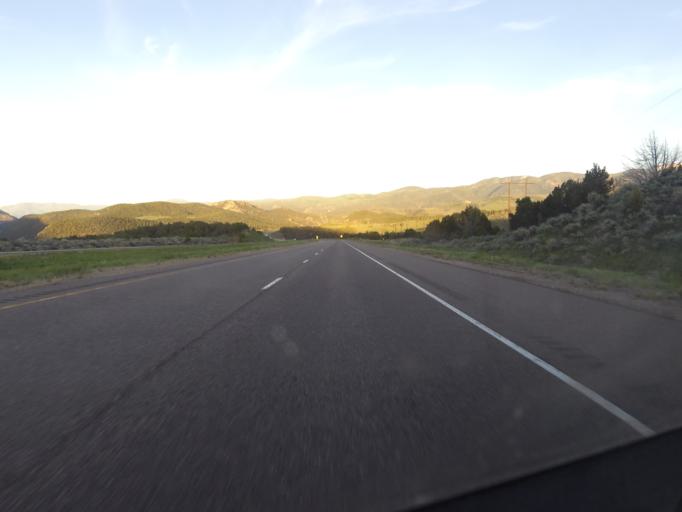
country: US
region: Utah
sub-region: Beaver County
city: Beaver
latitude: 38.5762
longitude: -112.4721
